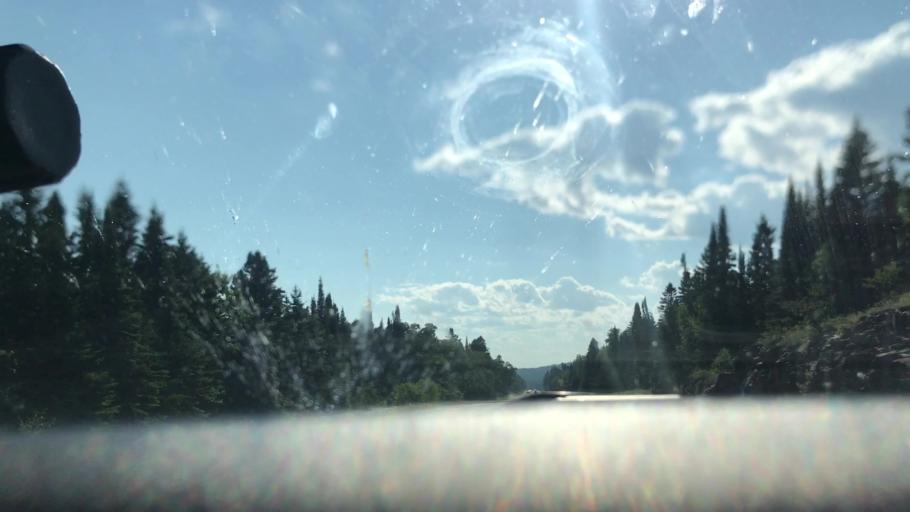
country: US
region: Minnesota
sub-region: Cook County
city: Grand Marais
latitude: 47.7963
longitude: -90.1282
